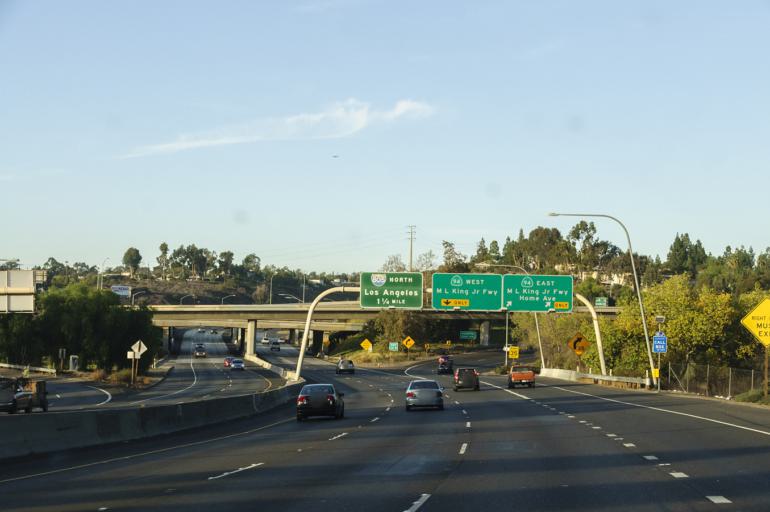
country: US
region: California
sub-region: San Diego County
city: San Diego
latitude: 32.7134
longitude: -117.1180
